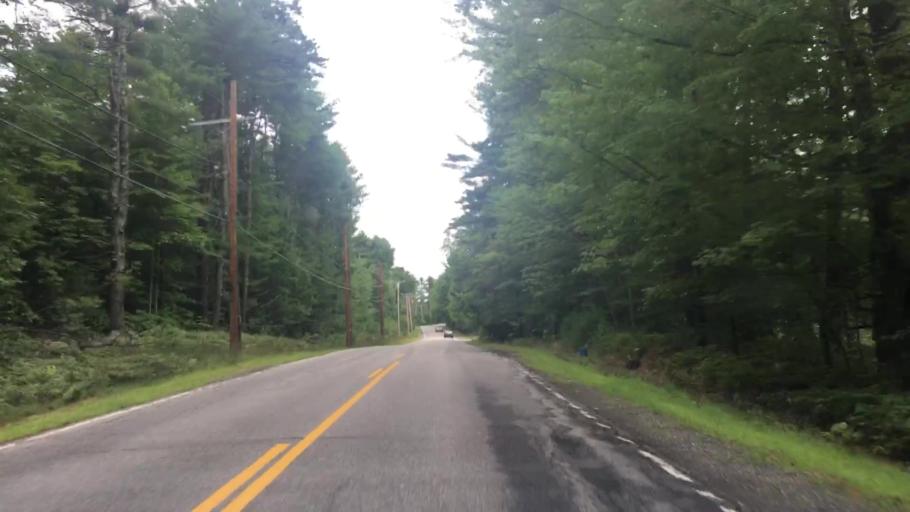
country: US
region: Maine
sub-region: York County
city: Lake Arrowhead
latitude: 43.6586
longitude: -70.7648
